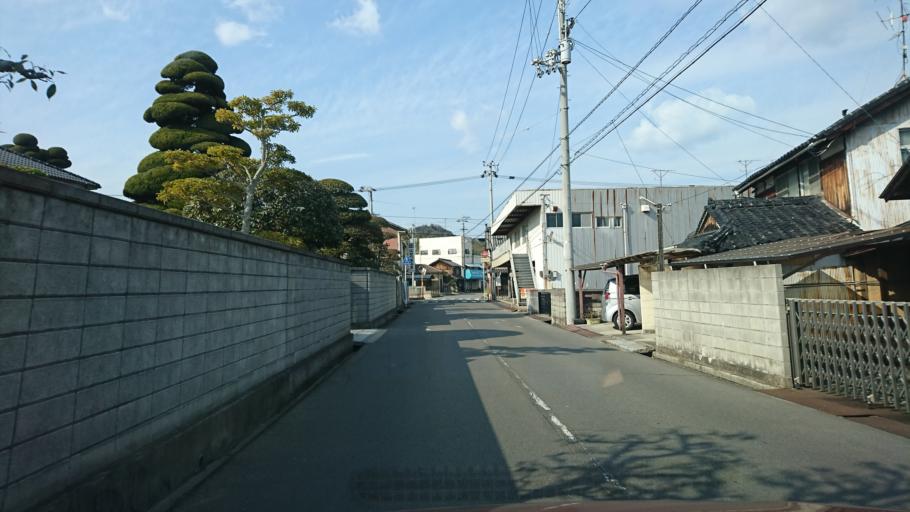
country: JP
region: Ehime
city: Saijo
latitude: 34.0210
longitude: 133.0399
